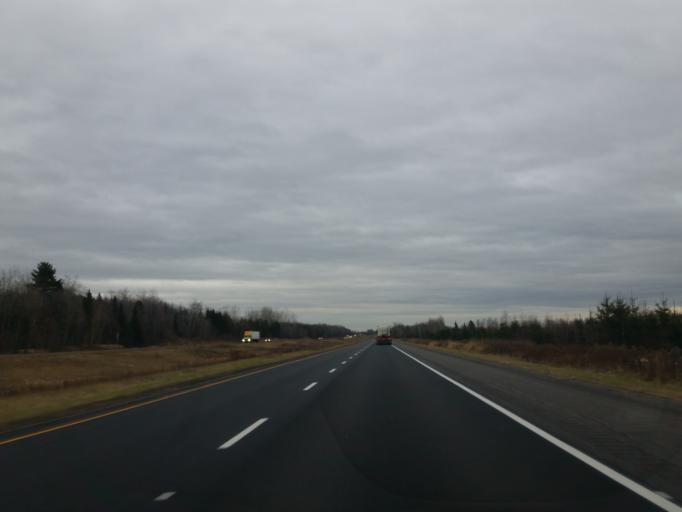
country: CA
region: Quebec
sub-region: Capitale-Nationale
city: Saint-Marc-des-Carrieres
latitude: 46.6053
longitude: -72.1050
